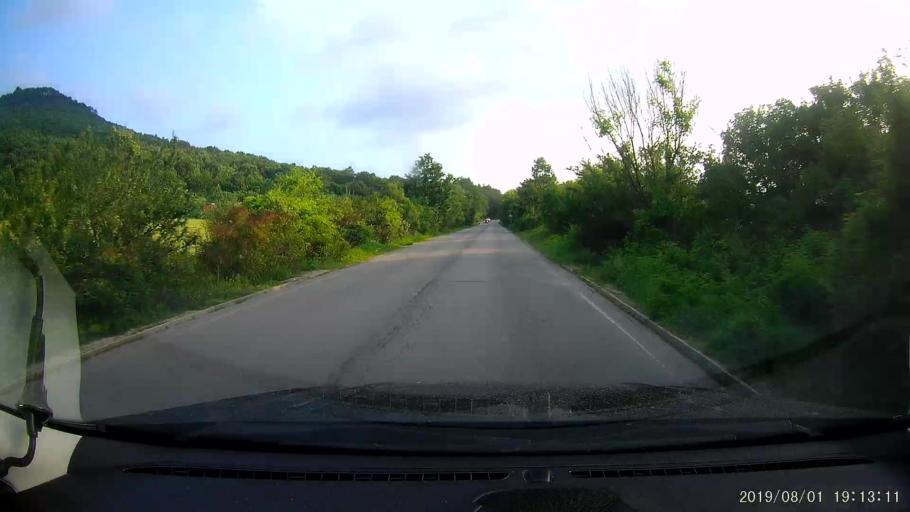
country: BG
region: Shumen
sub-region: Obshtina Smyadovo
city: Smyadovo
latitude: 42.9545
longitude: 26.9427
